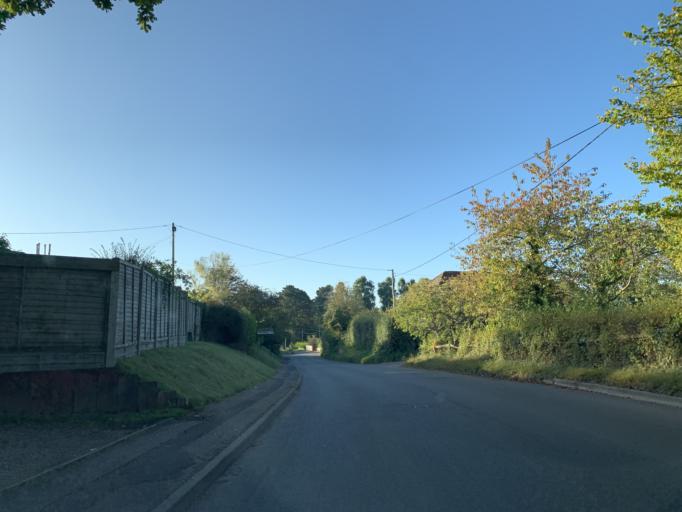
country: GB
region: England
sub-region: Wiltshire
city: Whiteparish
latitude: 50.9805
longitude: -1.6376
